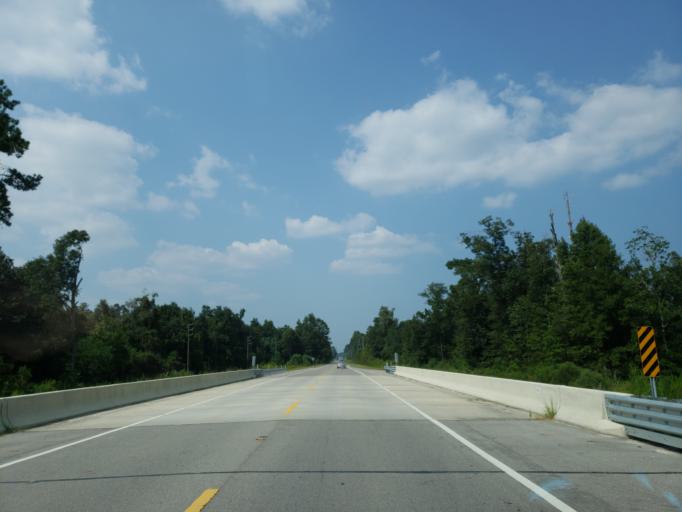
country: US
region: Mississippi
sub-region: Forrest County
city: Glendale
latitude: 31.4655
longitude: -89.2840
